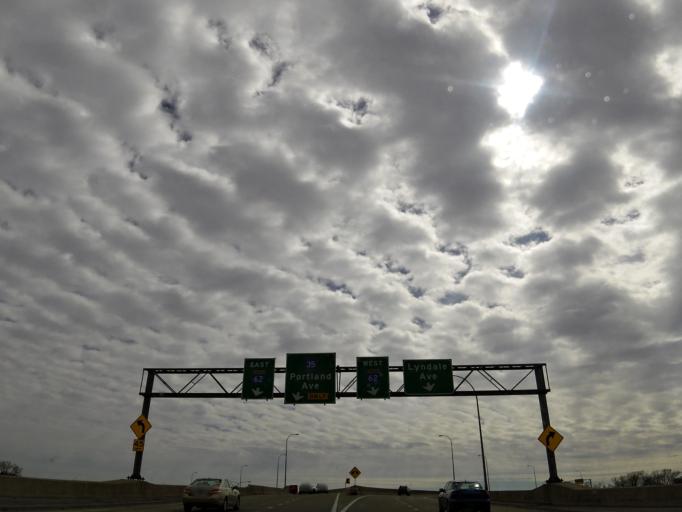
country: US
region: Minnesota
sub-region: Hennepin County
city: Richfield
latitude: 44.8934
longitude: -93.2755
